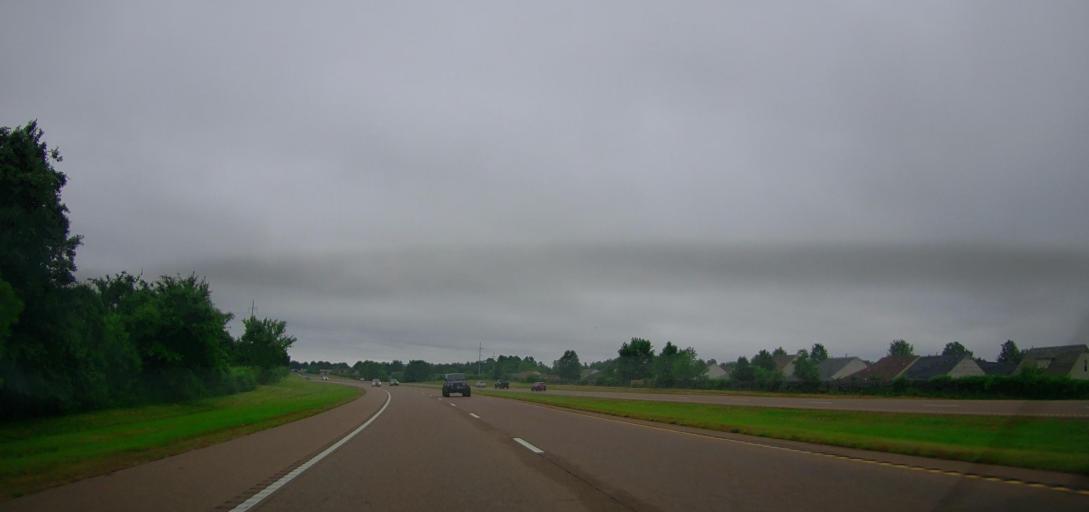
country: US
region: Mississippi
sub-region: De Soto County
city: Olive Branch
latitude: 34.9661
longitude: -89.8024
